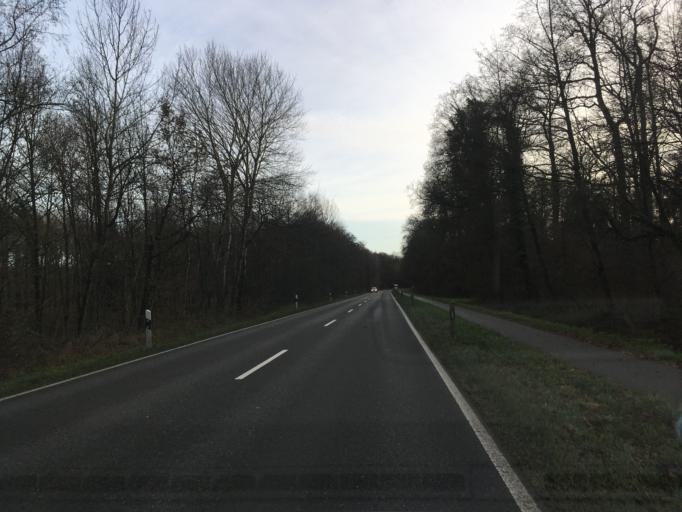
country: DE
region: North Rhine-Westphalia
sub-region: Regierungsbezirk Munster
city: Ahaus
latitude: 52.0423
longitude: 7.0194
